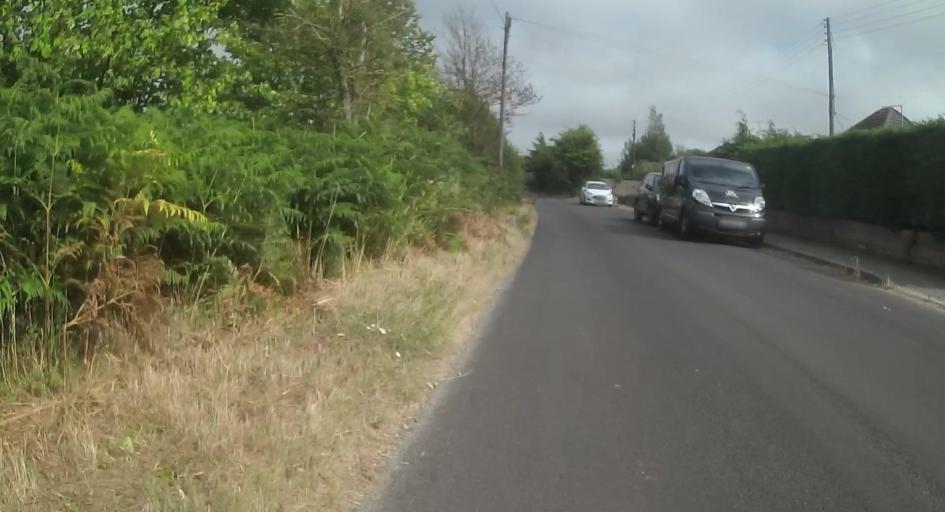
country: GB
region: England
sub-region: Dorset
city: Wool
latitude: 50.6809
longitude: -2.2341
